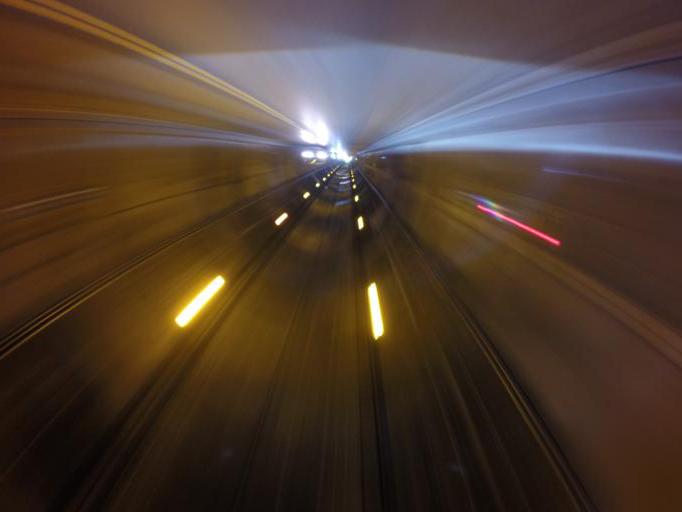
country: JP
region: Shizuoka
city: Shimoda
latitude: 34.8307
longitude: 138.9331
